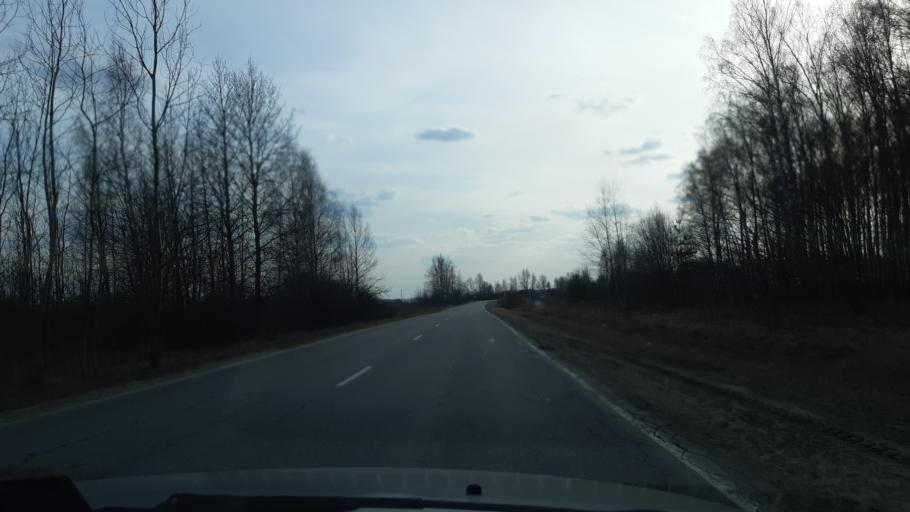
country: RU
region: Vladimir
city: Luknovo
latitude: 56.1929
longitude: 42.0289
